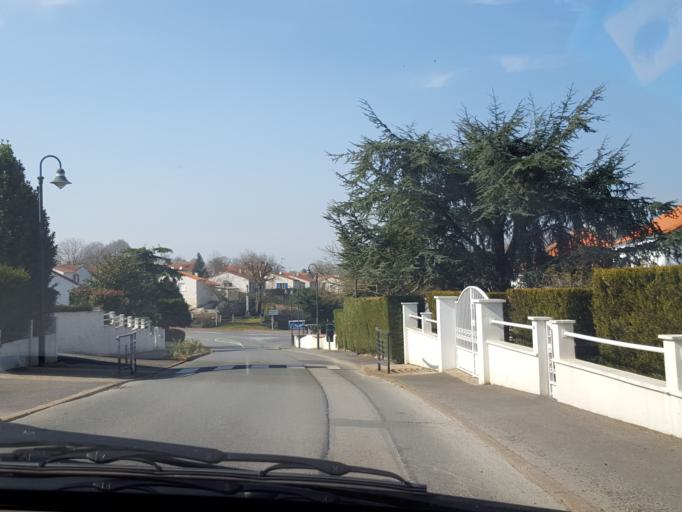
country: FR
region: Pays de la Loire
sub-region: Departement de la Vendee
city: Chavagnes-en-Paillers
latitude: 46.8623
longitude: -1.2602
